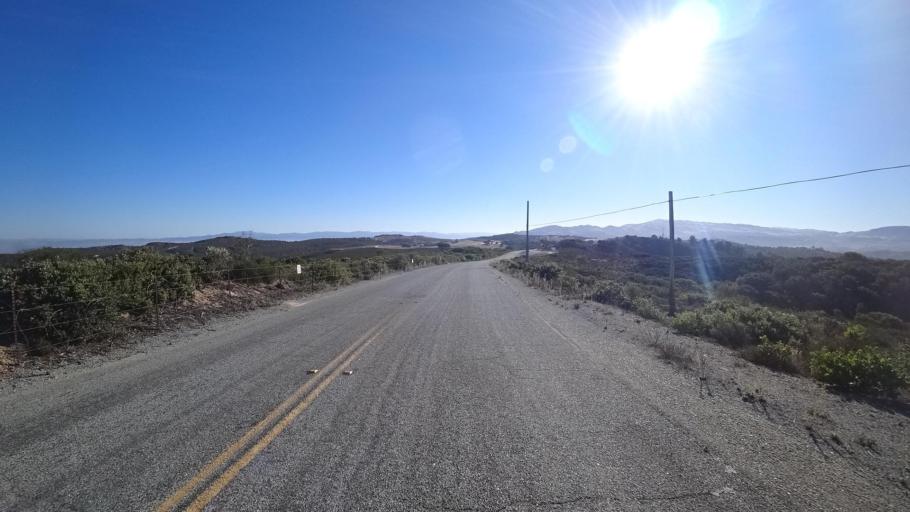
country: US
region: California
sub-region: Monterey County
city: Del Rey Oaks
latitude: 36.5867
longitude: -121.7691
